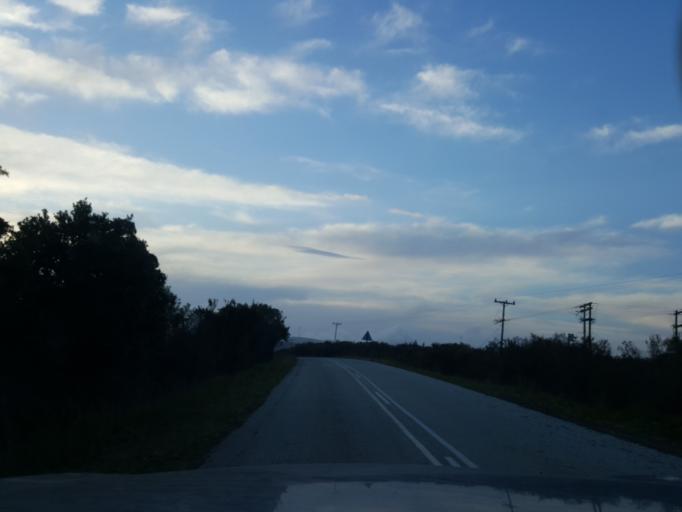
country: ZA
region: Eastern Cape
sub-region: Cacadu District Municipality
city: Grahamstown
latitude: -33.3923
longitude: 26.4751
